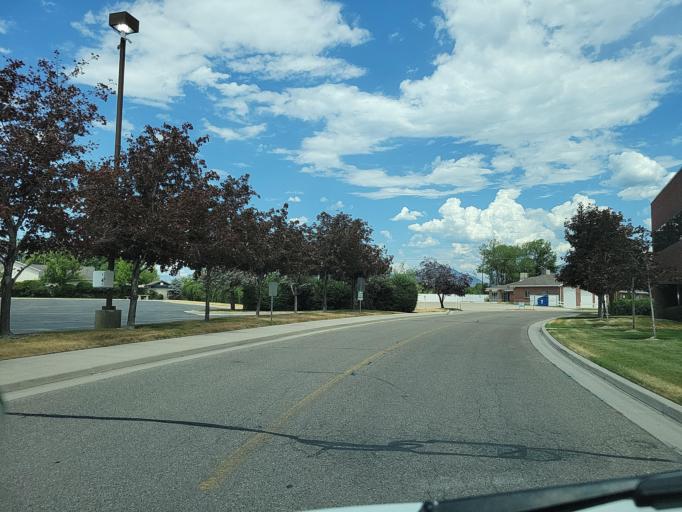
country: US
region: Utah
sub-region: Salt Lake County
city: Murray
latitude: 40.6401
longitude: -111.8845
